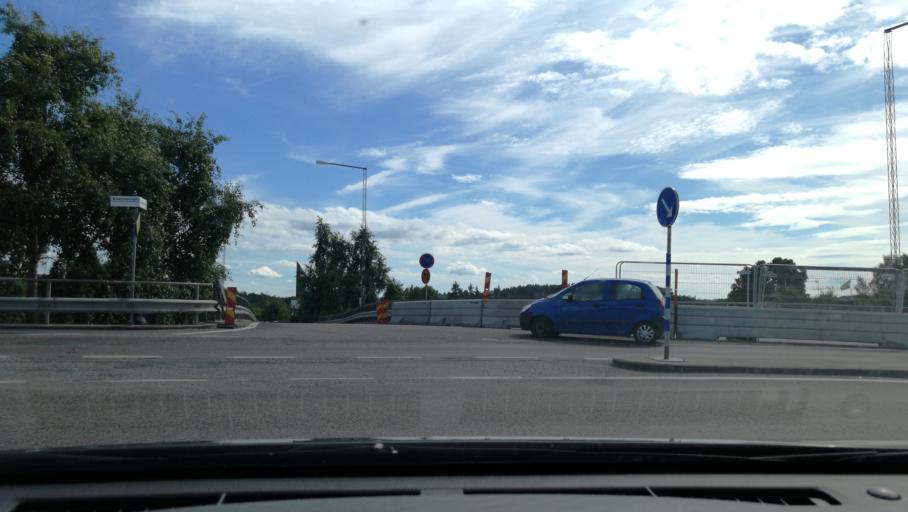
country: SE
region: Stockholm
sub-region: Stockholms Kommun
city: Kista
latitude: 59.3746
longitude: 17.9267
